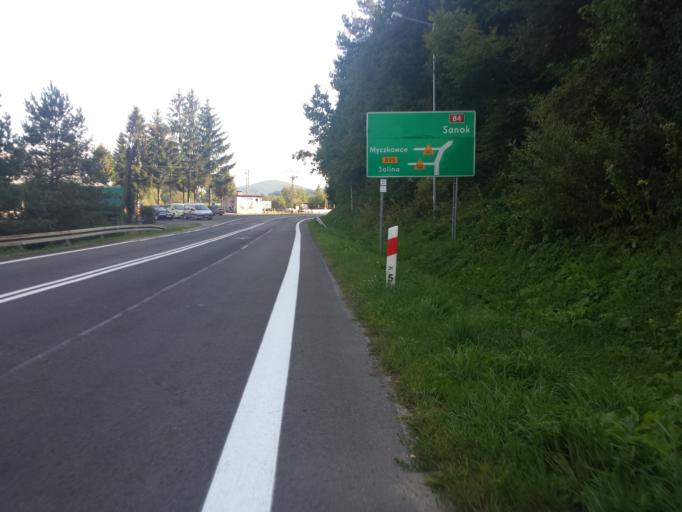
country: PL
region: Subcarpathian Voivodeship
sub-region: Powiat leski
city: Uherce Mineralne
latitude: 49.4659
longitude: 22.3990
